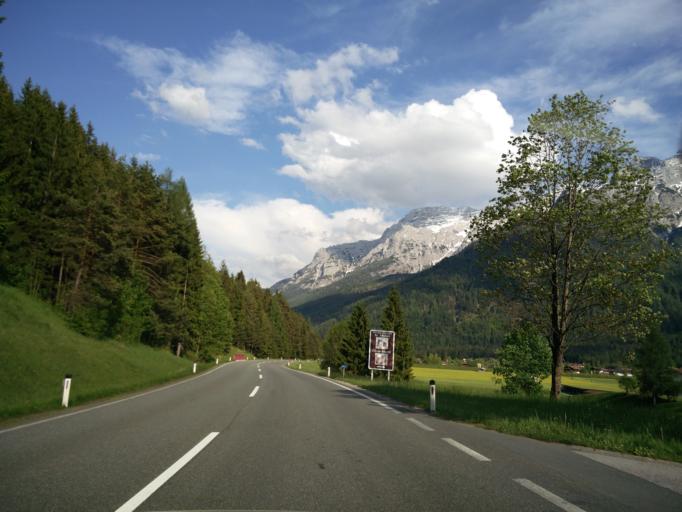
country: AT
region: Tyrol
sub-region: Politischer Bezirk Kitzbuhel
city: Waidring
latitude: 47.5872
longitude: 12.5735
